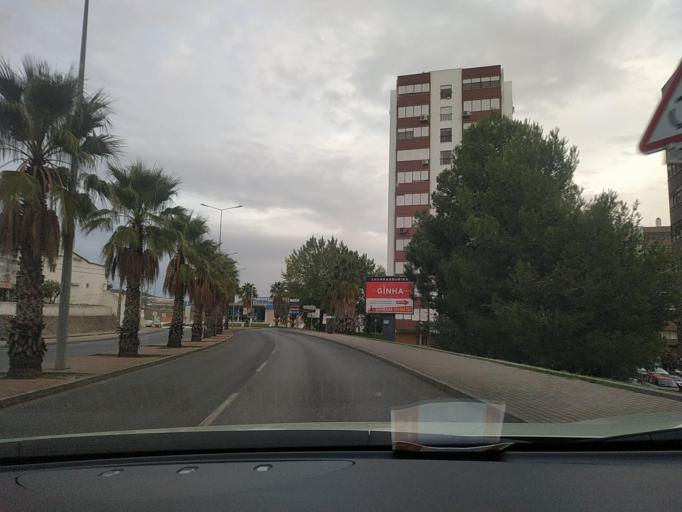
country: PT
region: Lisbon
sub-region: Loures
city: Loures
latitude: 38.8423
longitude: -9.1628
